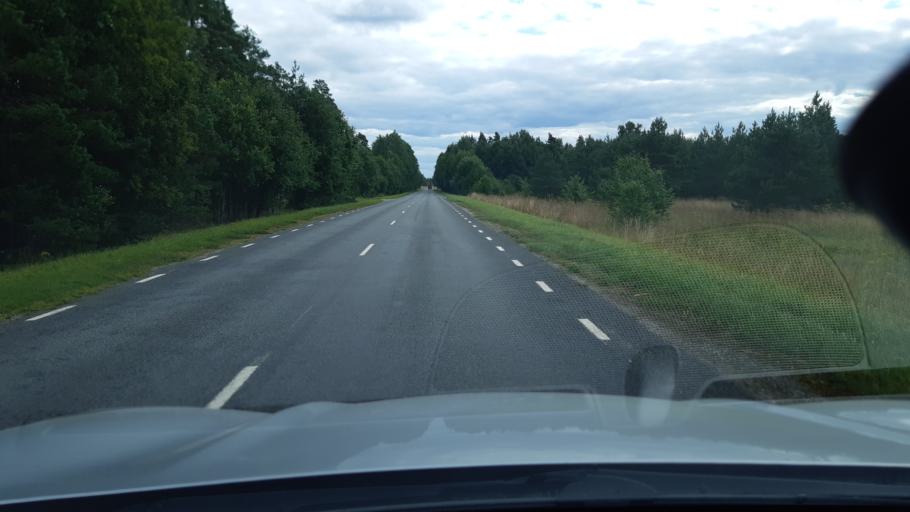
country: EE
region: Raplamaa
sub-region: Maerjamaa vald
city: Marjamaa
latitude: 59.0259
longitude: 24.5558
